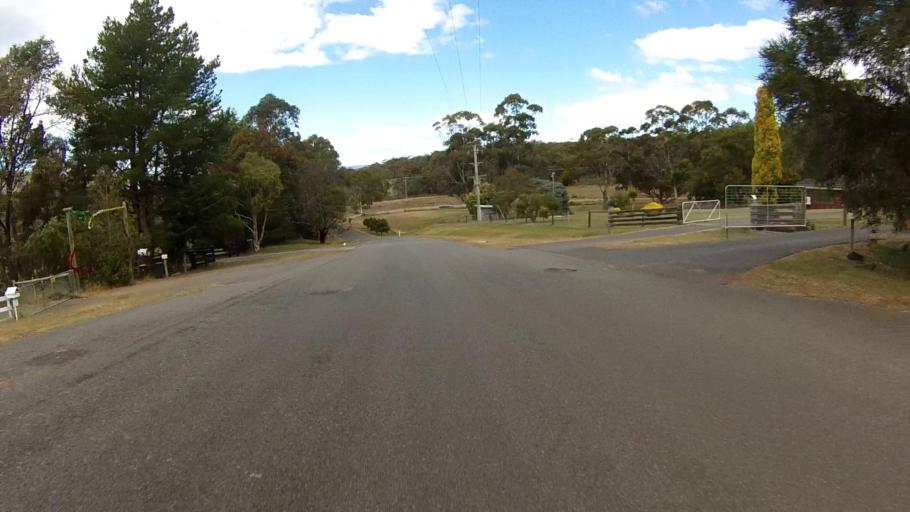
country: AU
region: Tasmania
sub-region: Clarence
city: Acton Park
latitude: -42.8711
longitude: 147.4724
